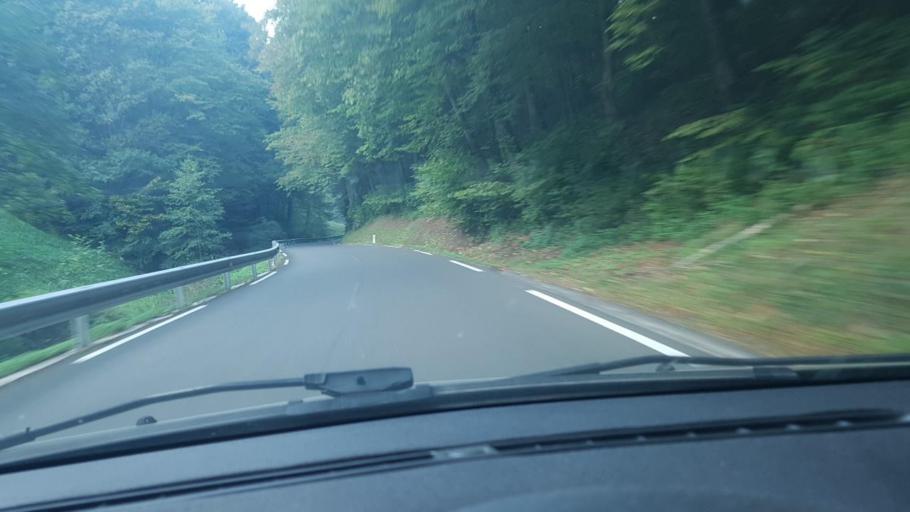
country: SI
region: Rogatec
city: Rogatec
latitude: 46.2736
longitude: 15.7121
